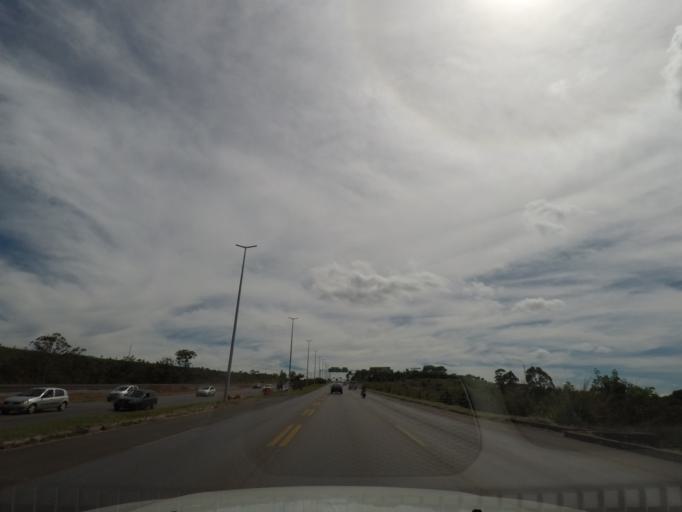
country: BR
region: Federal District
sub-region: Brasilia
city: Brasilia
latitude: -15.6924
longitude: -47.8675
